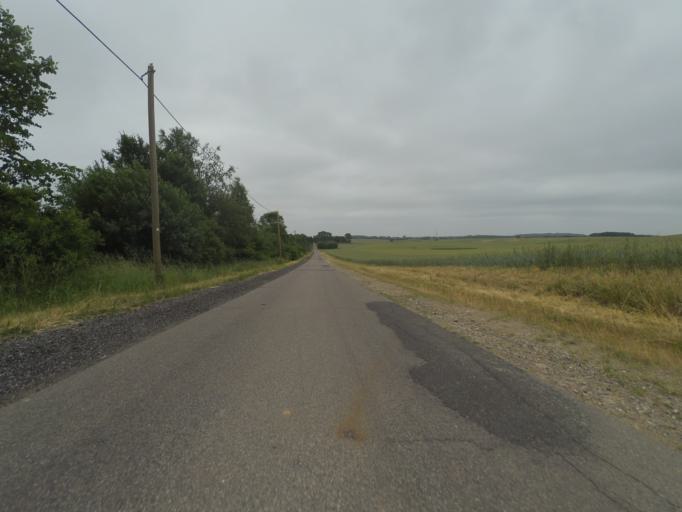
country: DE
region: Mecklenburg-Vorpommern
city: Gaegelow
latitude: 53.6982
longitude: 11.8637
